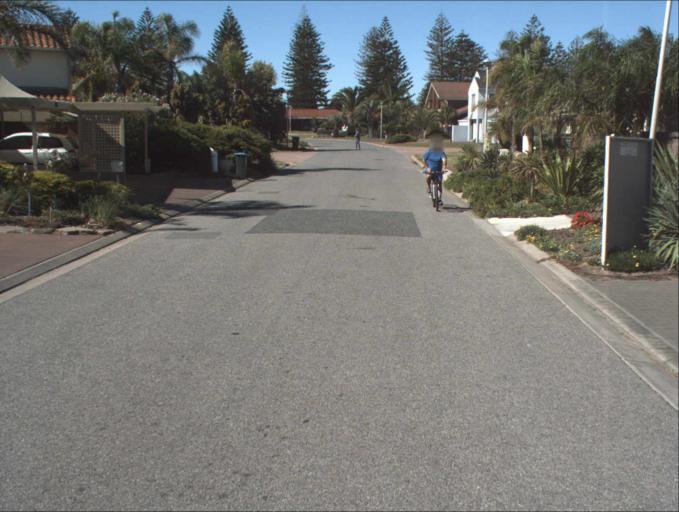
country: AU
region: South Australia
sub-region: Port Adelaide Enfield
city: Birkenhead
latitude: -34.7845
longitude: 138.4869
